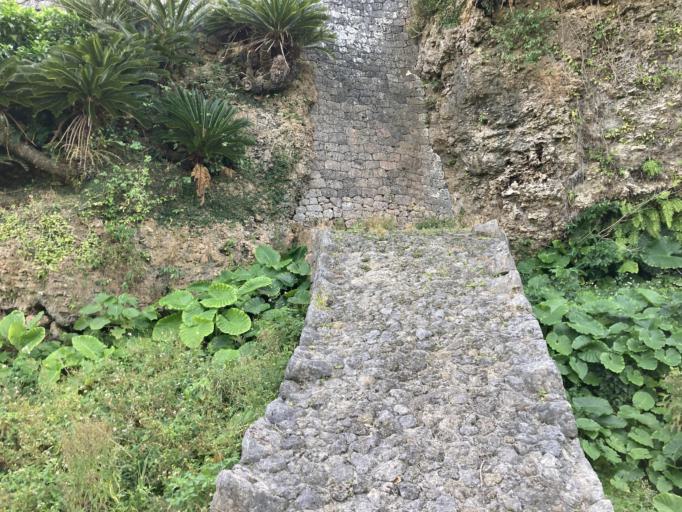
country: JP
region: Okinawa
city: Katsuren-haebaru
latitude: 26.3308
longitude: 127.8792
